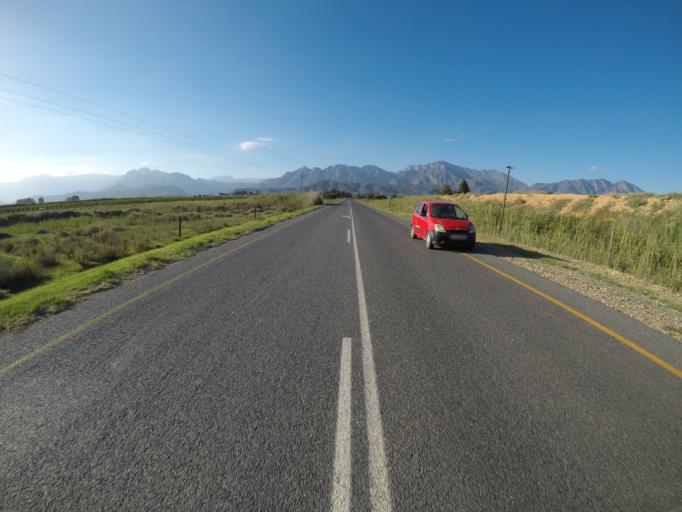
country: ZA
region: Western Cape
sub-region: Cape Winelands District Municipality
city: Worcester
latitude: -33.6696
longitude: 19.5426
